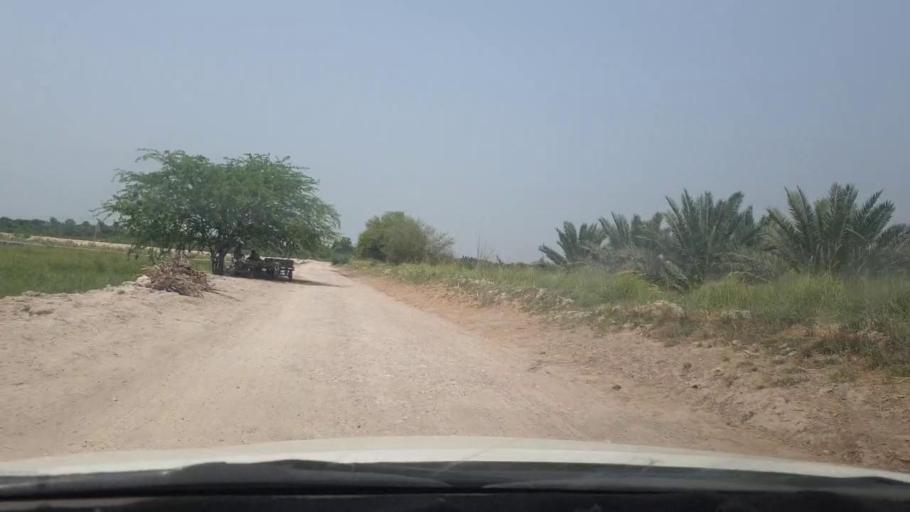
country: PK
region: Sindh
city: Khairpur
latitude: 27.5017
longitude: 68.8699
